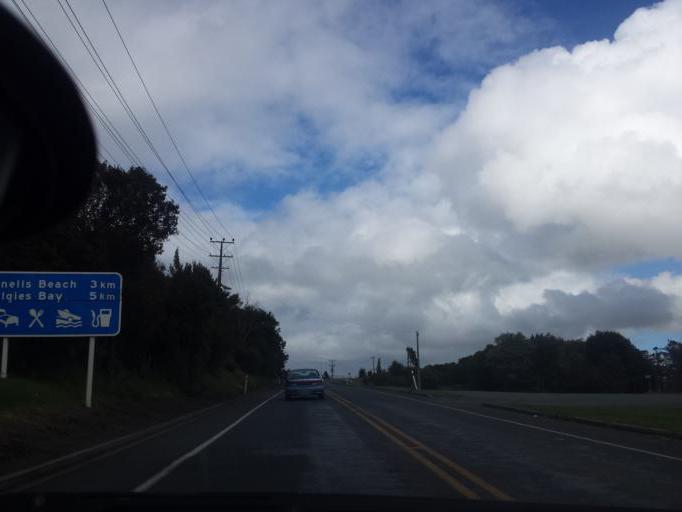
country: NZ
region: Auckland
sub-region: Auckland
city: Warkworth
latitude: -36.3994
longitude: 174.7094
